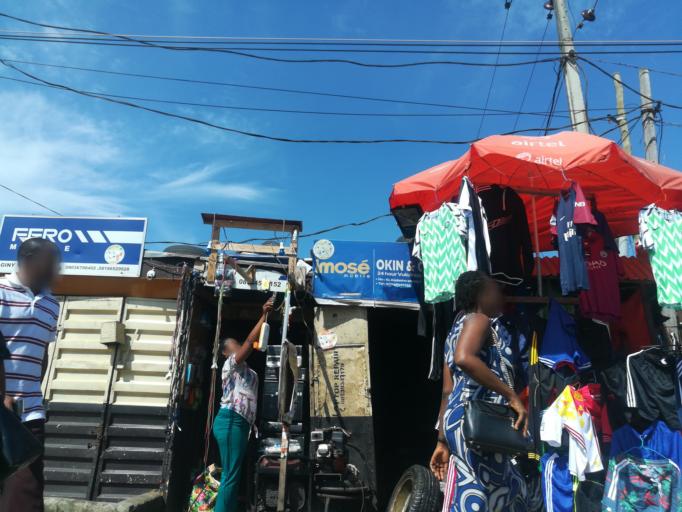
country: NG
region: Lagos
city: Ikeja
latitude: 6.5940
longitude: 3.3419
